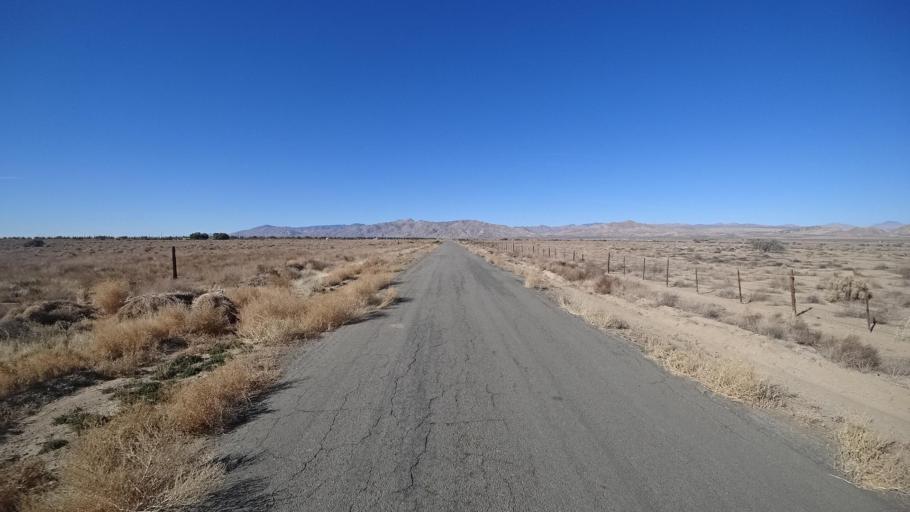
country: US
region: California
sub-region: Kern County
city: California City
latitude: 35.2870
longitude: -117.9271
